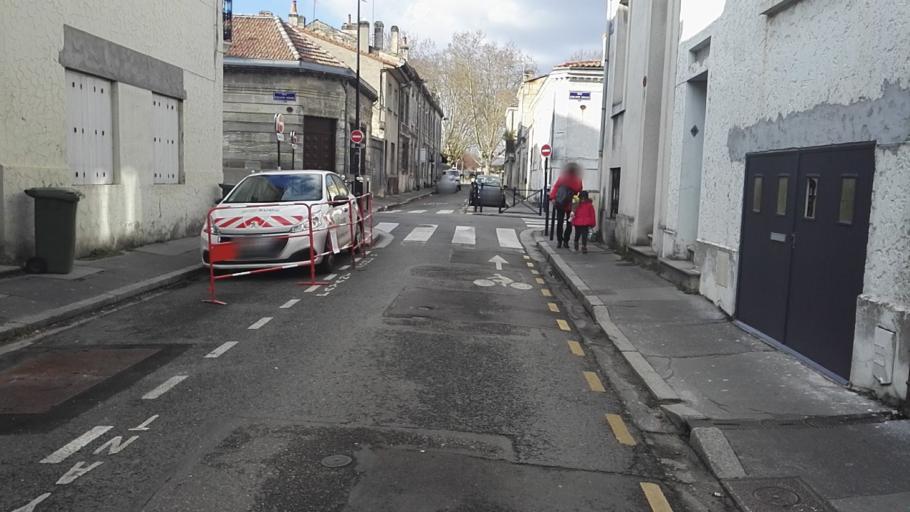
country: FR
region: Aquitaine
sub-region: Departement de la Gironde
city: Bordeaux
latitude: 44.8319
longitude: -0.5938
